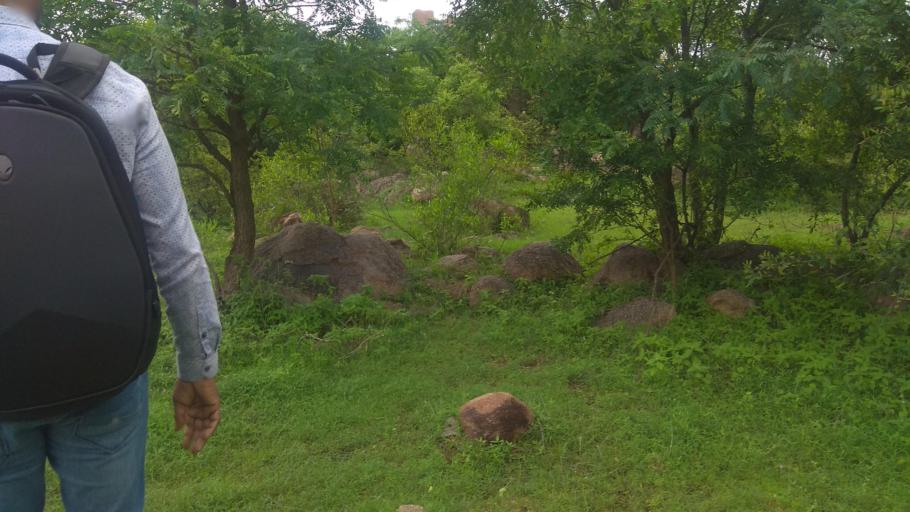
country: IN
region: Telangana
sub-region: Mahbubnagar
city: Farrukhnagar
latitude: 16.8978
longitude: 78.4954
